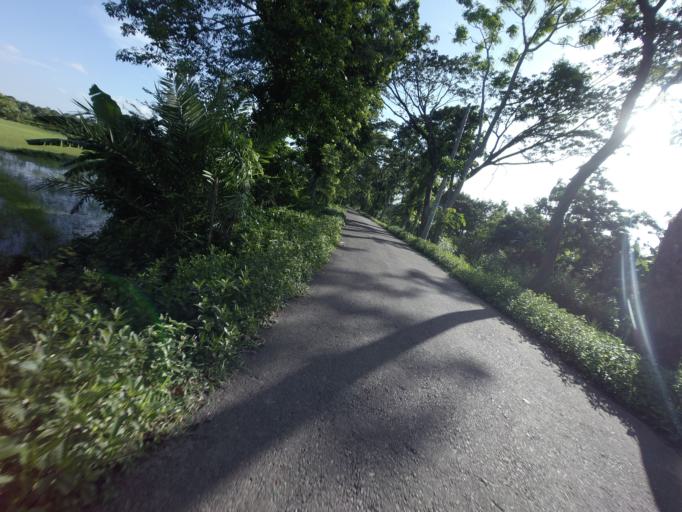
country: BD
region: Khulna
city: Bhatpara Abhaynagar
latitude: 22.9437
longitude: 89.5265
